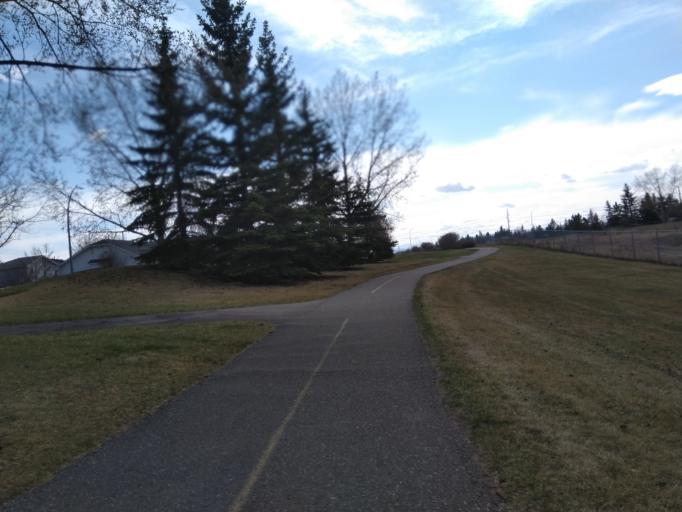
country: CA
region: Alberta
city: Chestermere
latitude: 51.0491
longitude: -113.9318
